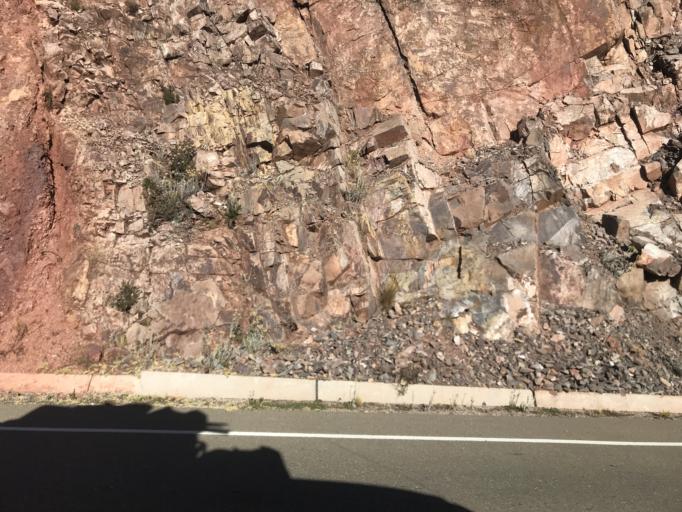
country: BO
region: La Paz
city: San Pedro
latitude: -16.1927
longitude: -68.9151
